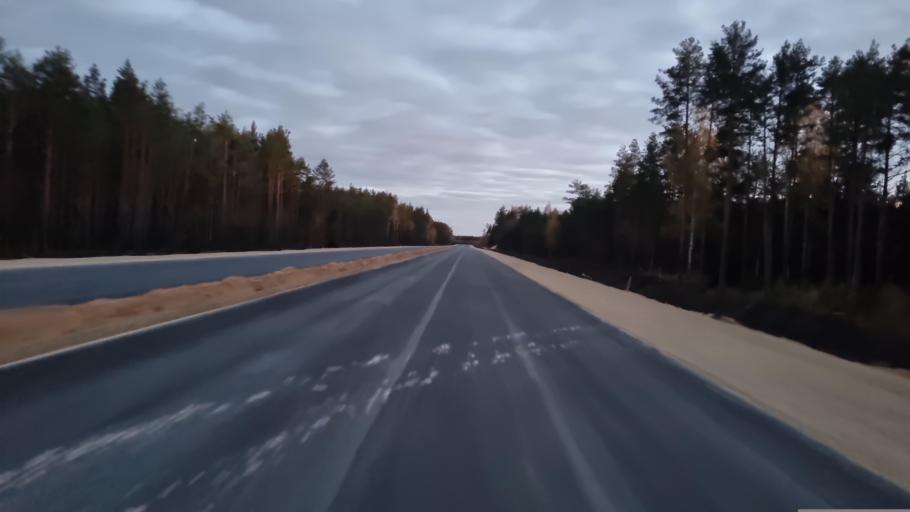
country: LV
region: Kekava
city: Balozi
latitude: 56.8507
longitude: 24.1569
